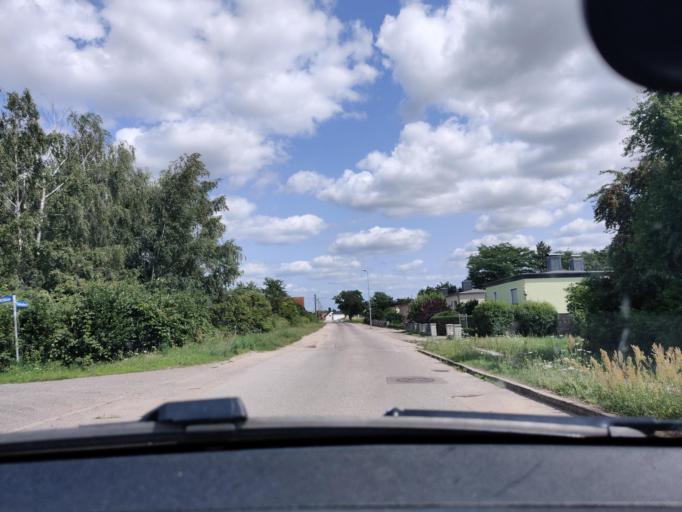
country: DE
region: Saxony-Anhalt
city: Leitzkau
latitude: 52.0604
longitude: 11.9531
